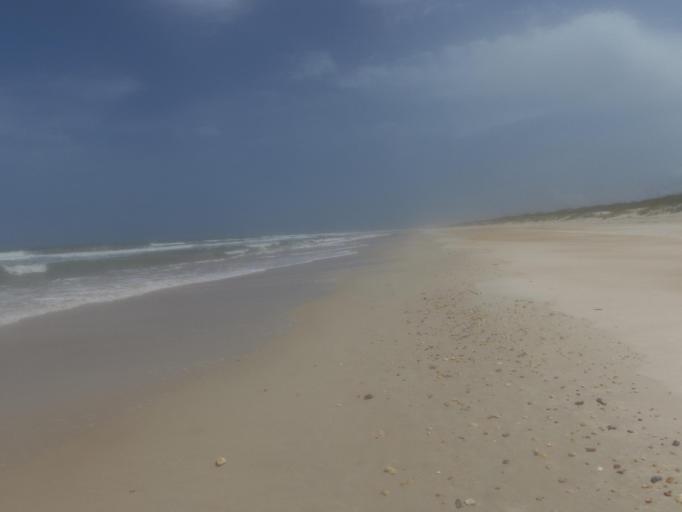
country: US
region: Florida
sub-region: Saint Johns County
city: Saint Augustine Beach
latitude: 29.8825
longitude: -81.2723
